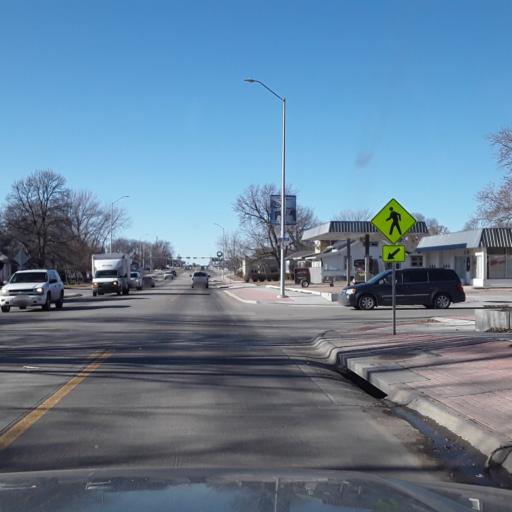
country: US
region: Nebraska
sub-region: Phelps County
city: Holdrege
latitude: 40.4380
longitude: -99.3762
